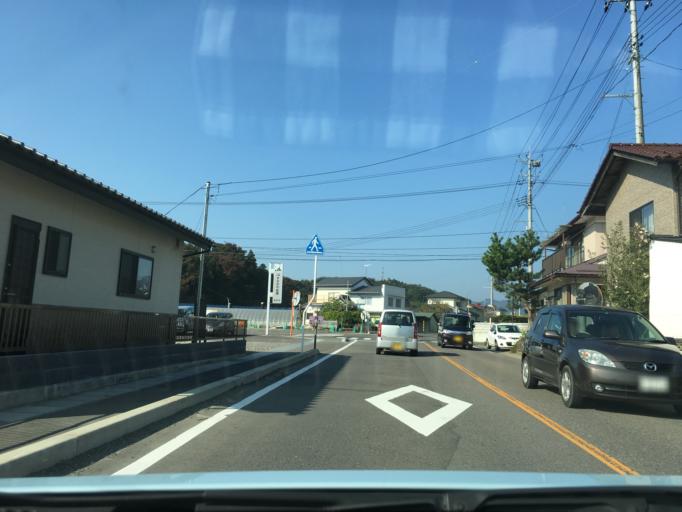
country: JP
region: Fukushima
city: Sukagawa
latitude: 37.2863
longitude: 140.2390
